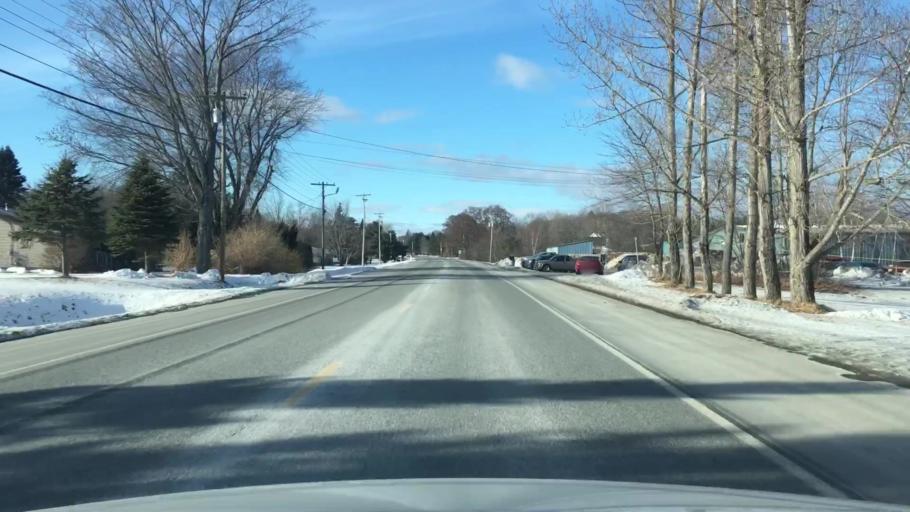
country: US
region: Maine
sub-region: Penobscot County
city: Eddington
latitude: 44.8241
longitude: -68.6527
